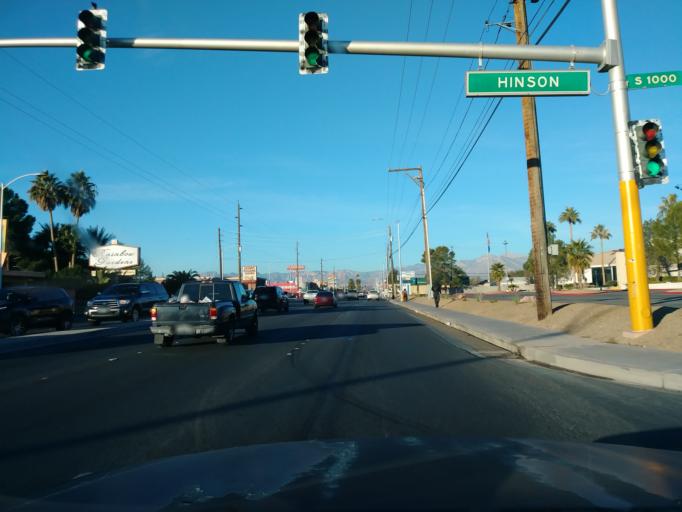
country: US
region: Nevada
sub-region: Clark County
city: Las Vegas
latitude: 36.1592
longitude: -115.1954
